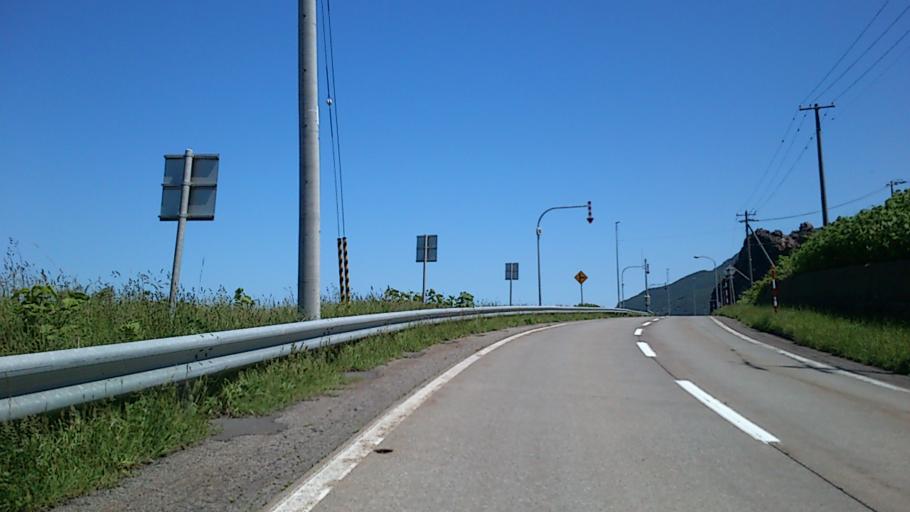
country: JP
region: Hokkaido
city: Rumoi
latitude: 43.7530
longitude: 141.3499
